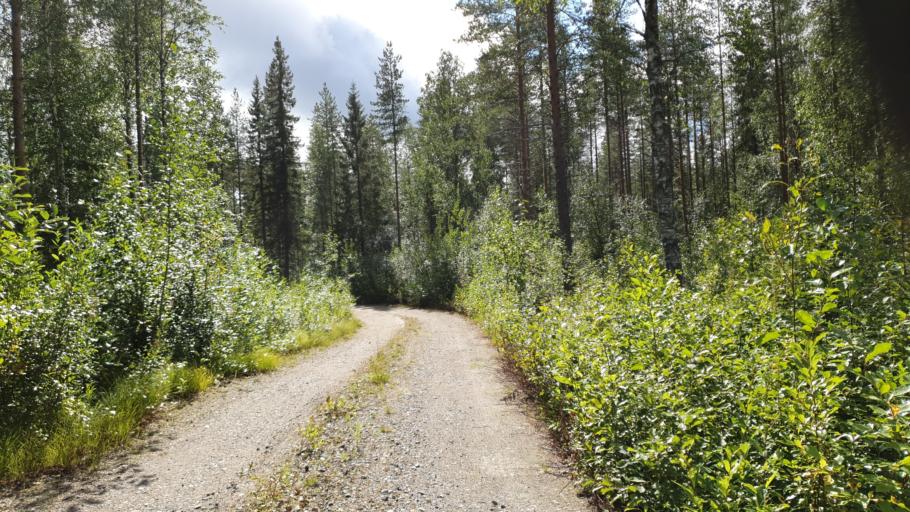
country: FI
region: Kainuu
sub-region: Kehys-Kainuu
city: Kuhmo
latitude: 64.1414
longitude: 29.3871
